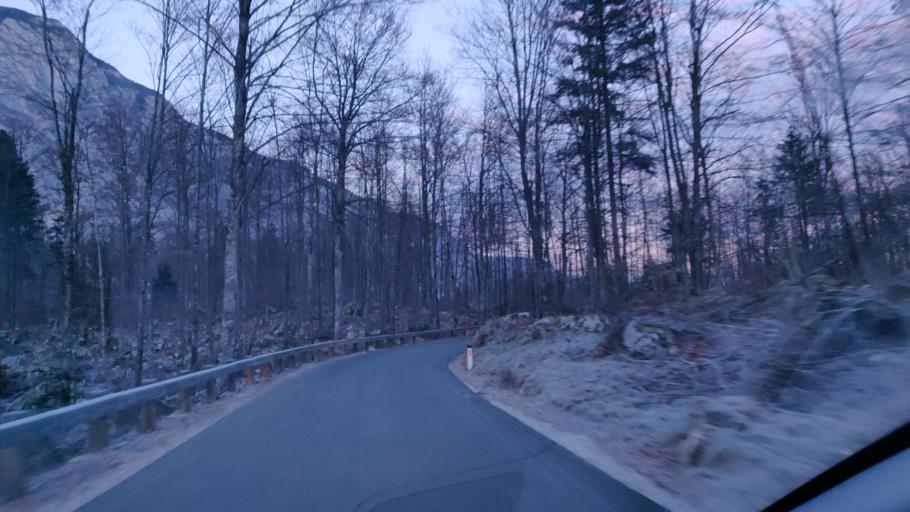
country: SI
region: Tolmin
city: Tolmin
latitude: 46.2762
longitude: 13.8209
